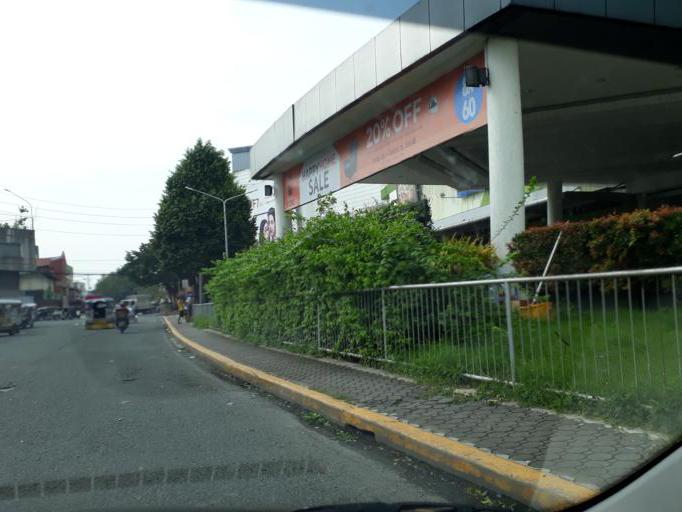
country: PH
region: Metro Manila
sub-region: City of Manila
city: Manila
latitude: 14.6175
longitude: 120.9853
